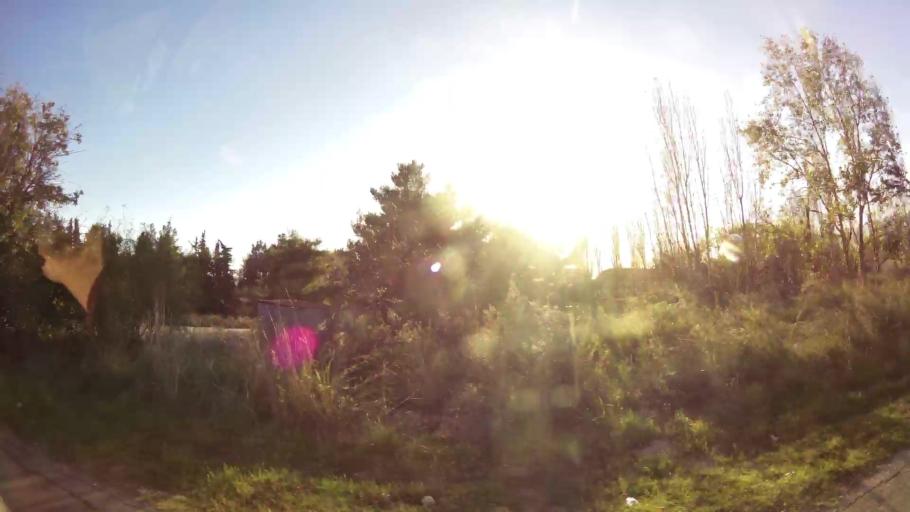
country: GR
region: Attica
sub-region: Nomarchia Anatolikis Attikis
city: Anoixi
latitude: 38.1335
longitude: 23.8524
